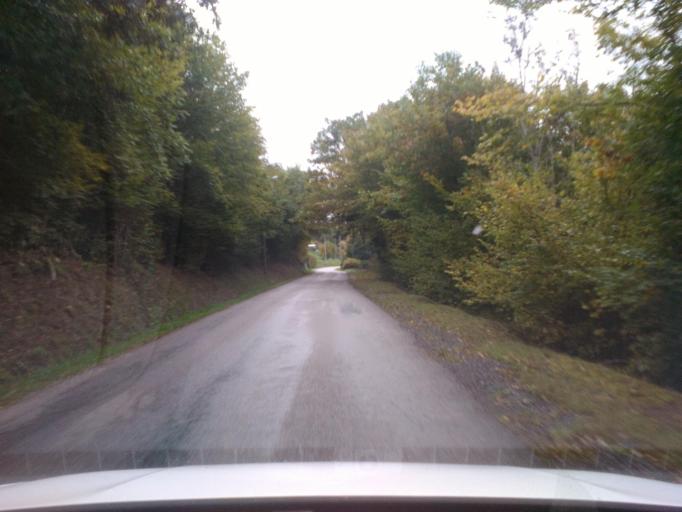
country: FR
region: Lorraine
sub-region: Departement des Vosges
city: Moyenmoutier
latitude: 48.3755
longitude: 6.9175
